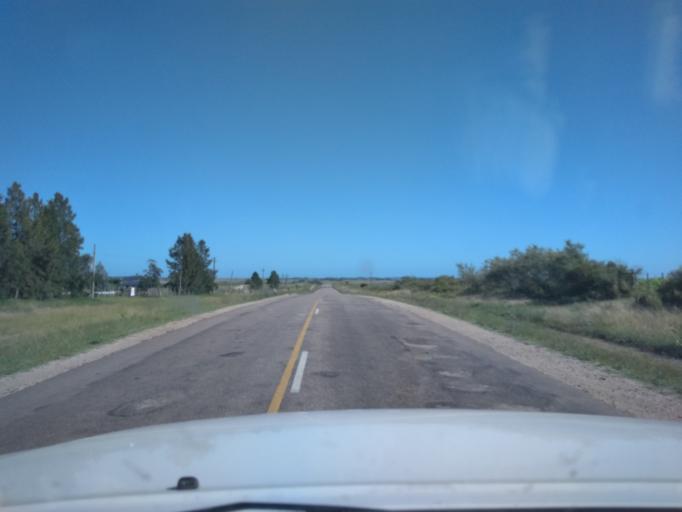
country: UY
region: Canelones
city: San Ramon
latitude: -34.2392
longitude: -55.9260
